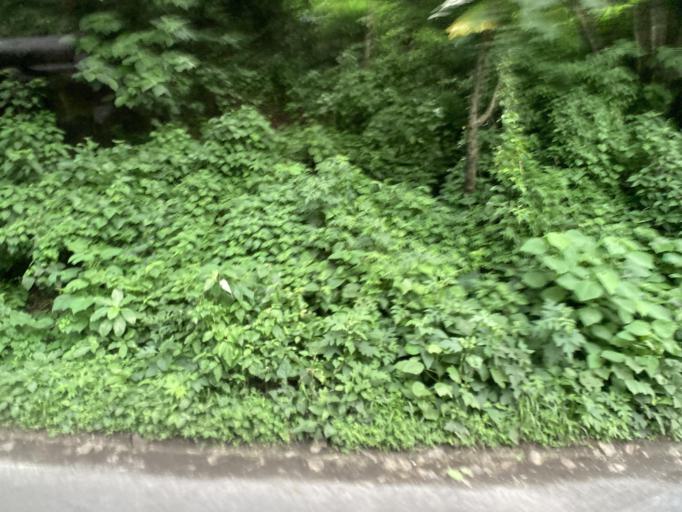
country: GT
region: Guatemala
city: Villa Canales
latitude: 14.4305
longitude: -90.5352
